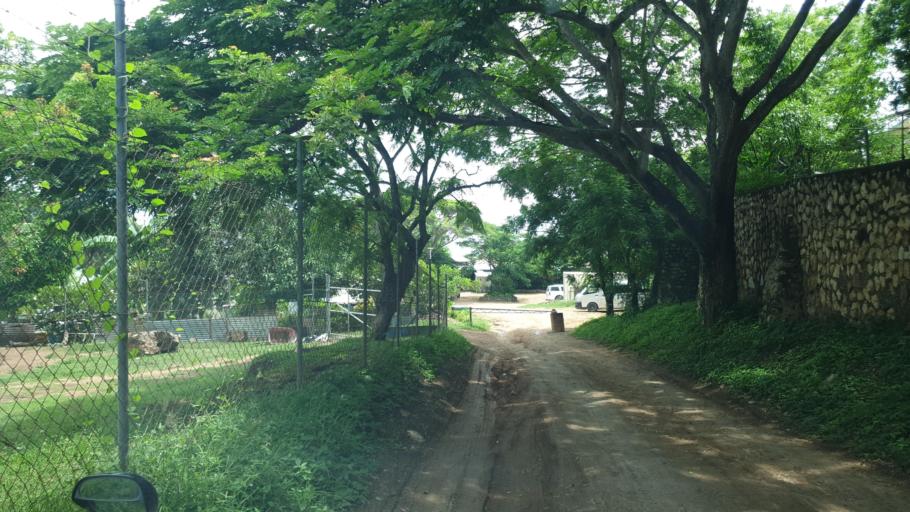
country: PG
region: National Capital
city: Port Moresby
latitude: -9.5276
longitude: 147.2499
